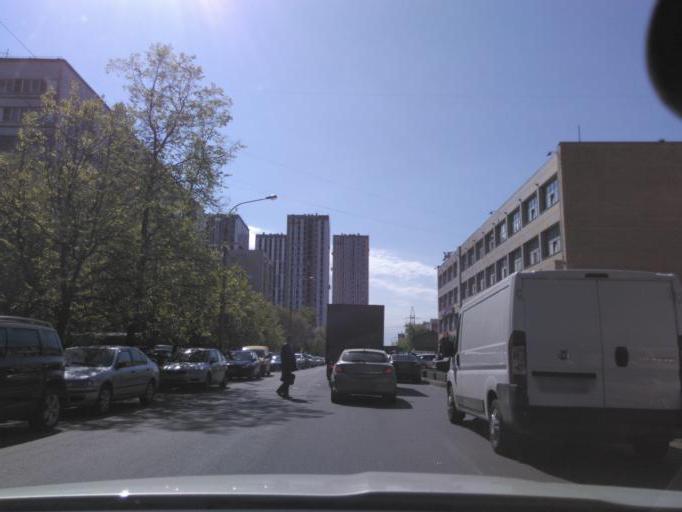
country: RU
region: Moskovskaya
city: Levoberezhnyy
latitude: 55.8440
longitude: 37.4910
